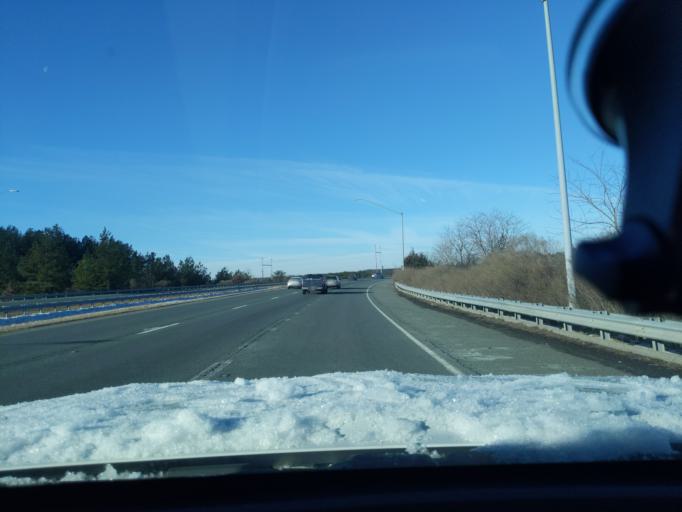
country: US
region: Maryland
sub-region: Anne Arundel County
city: Severn
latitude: 39.1485
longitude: -76.6931
